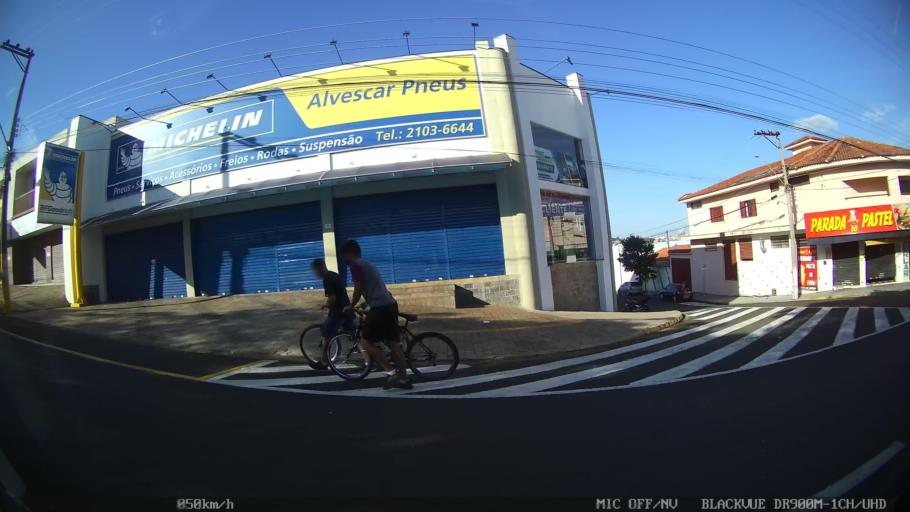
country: BR
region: Sao Paulo
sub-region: Franca
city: Franca
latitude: -20.5181
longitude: -47.3974
